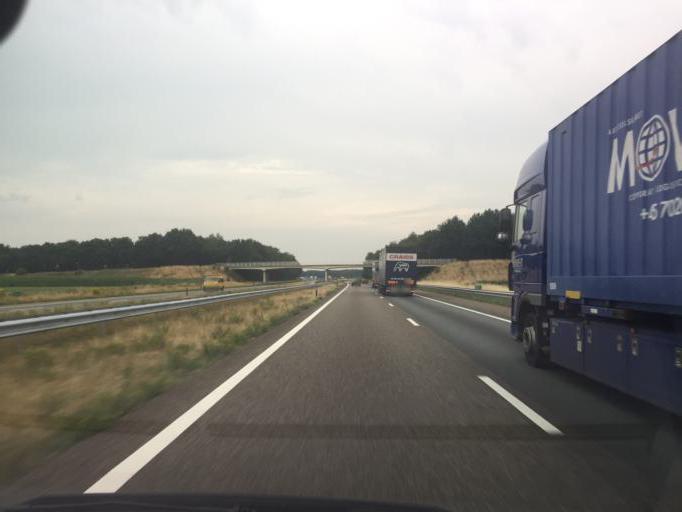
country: NL
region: Limburg
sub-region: Gemeente Leudal
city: Heythuysen
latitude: 51.3814
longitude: 5.8987
